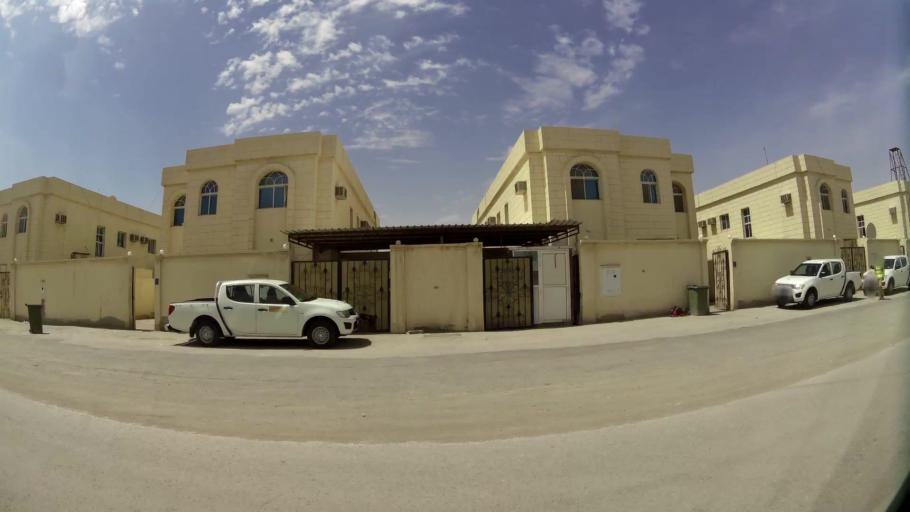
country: QA
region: Baladiyat ar Rayyan
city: Ar Rayyan
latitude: 25.2781
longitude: 51.4262
